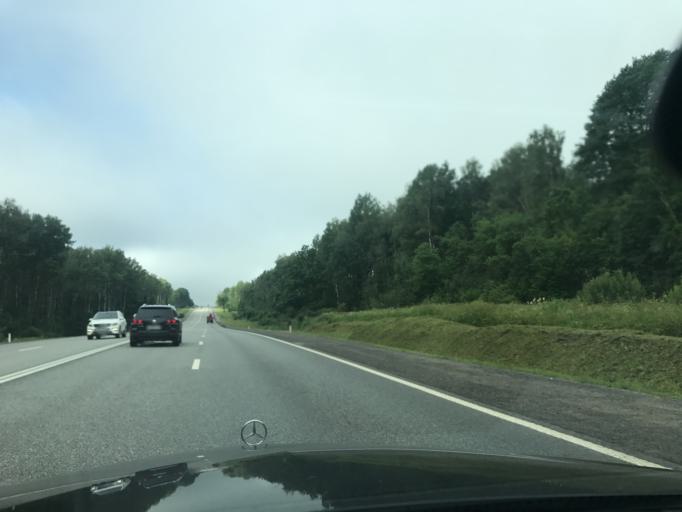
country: RU
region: Smolensk
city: Vyaz'ma
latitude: 55.3023
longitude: 34.4952
